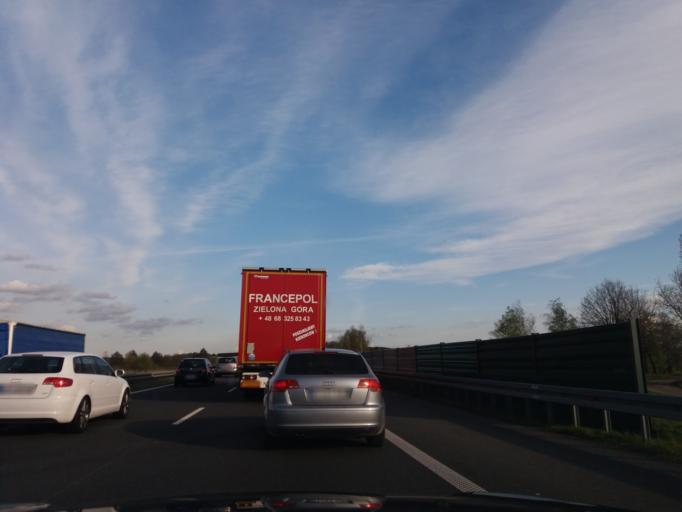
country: PL
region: Opole Voivodeship
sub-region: Powiat opolski
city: Niemodlin
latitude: 50.6817
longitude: 17.6448
